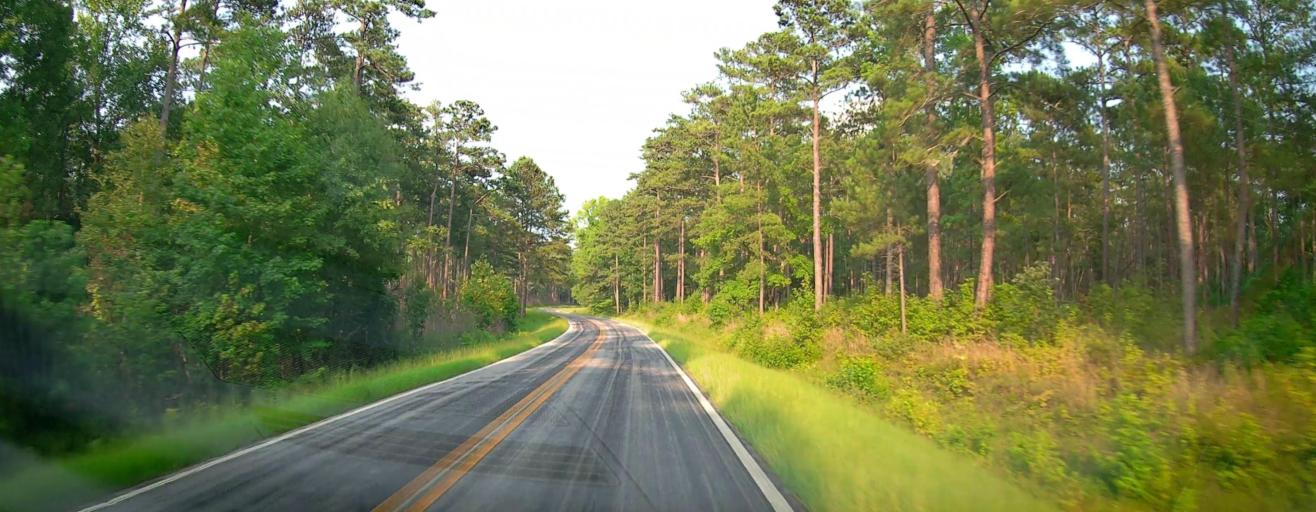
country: US
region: Georgia
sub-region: Jones County
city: Gray
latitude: 33.0961
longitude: -83.6929
